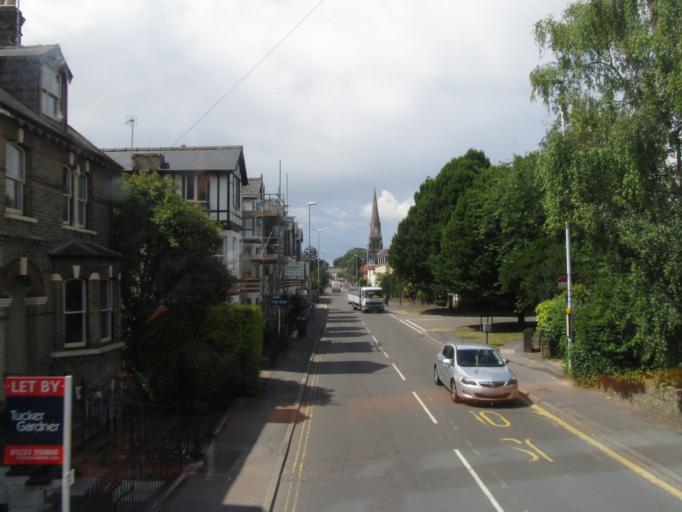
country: GB
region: England
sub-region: Cambridgeshire
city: Cambridge
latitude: 52.2149
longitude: 0.1202
